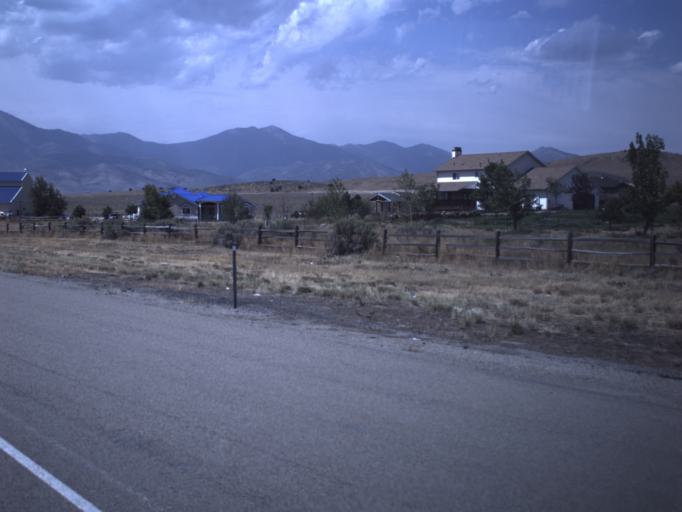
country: US
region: Utah
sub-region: Utah County
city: Eagle Mountain
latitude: 40.3766
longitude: -112.0084
